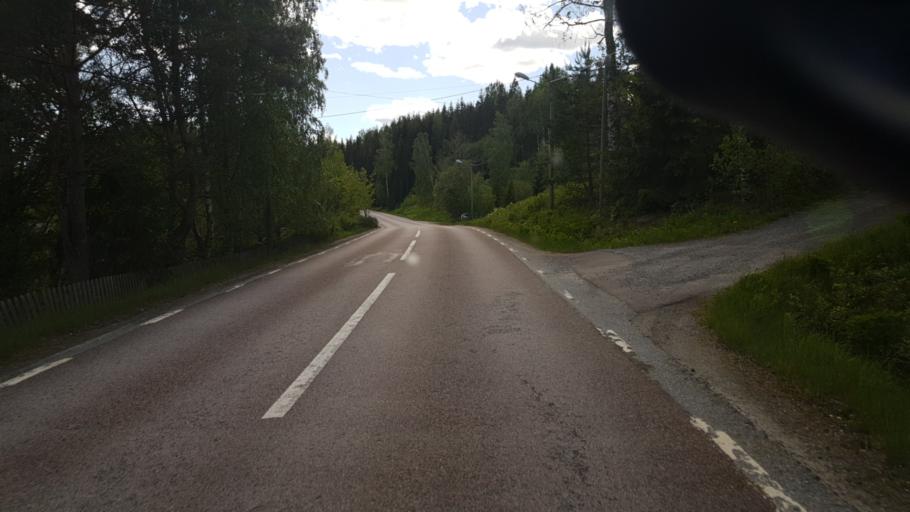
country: SE
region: Vaermland
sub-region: Sunne Kommun
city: Sunne
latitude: 59.6724
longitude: 13.0224
